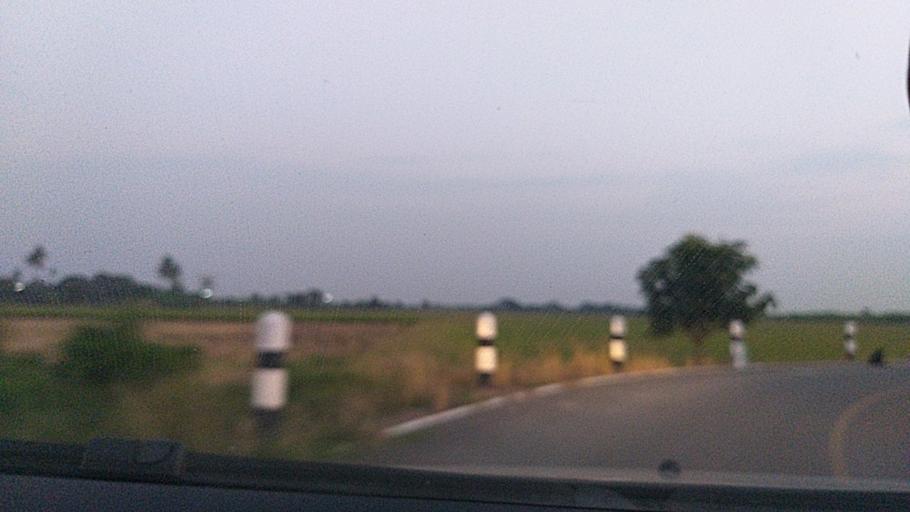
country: TH
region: Sing Buri
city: Phrom Buri
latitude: 14.8213
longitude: 100.4045
